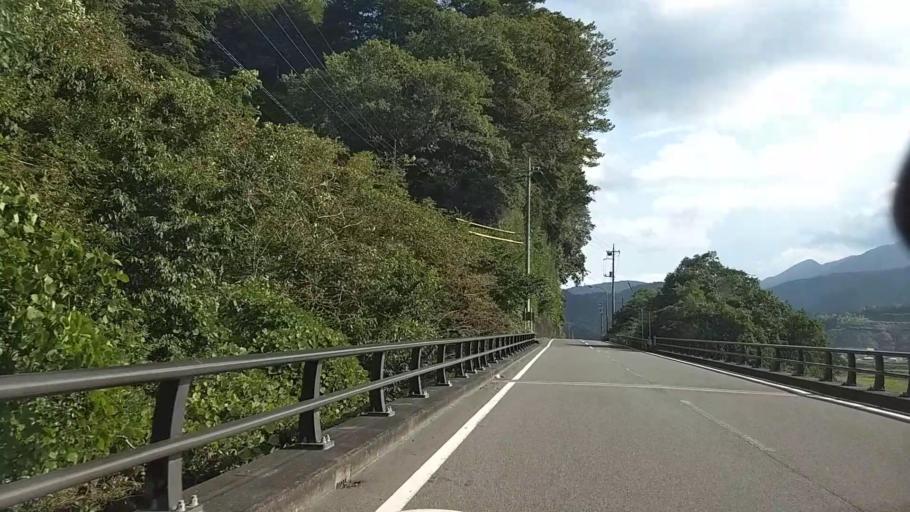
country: JP
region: Shizuoka
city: Fujinomiya
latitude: 35.2884
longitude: 138.4600
